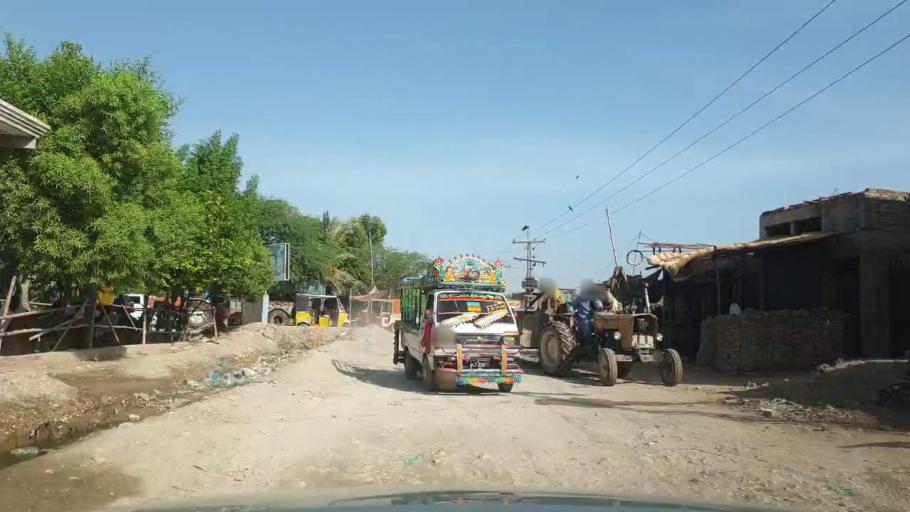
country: PK
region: Sindh
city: Rohri
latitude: 27.6787
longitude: 68.8797
